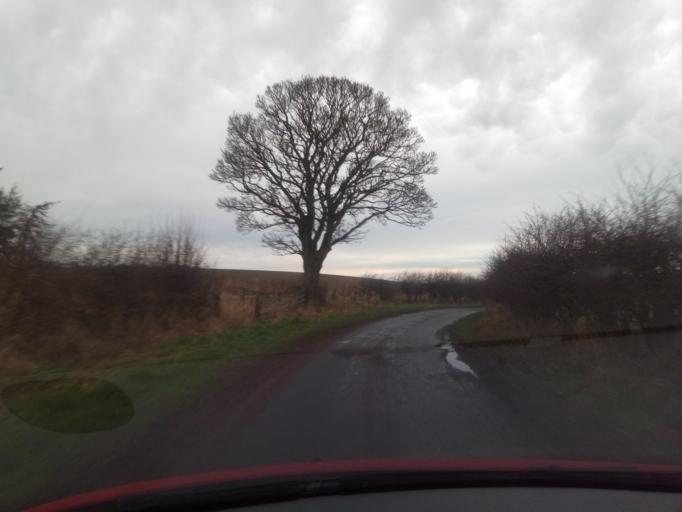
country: GB
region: England
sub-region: Northumberland
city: Wooler
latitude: 55.5017
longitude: -1.9396
